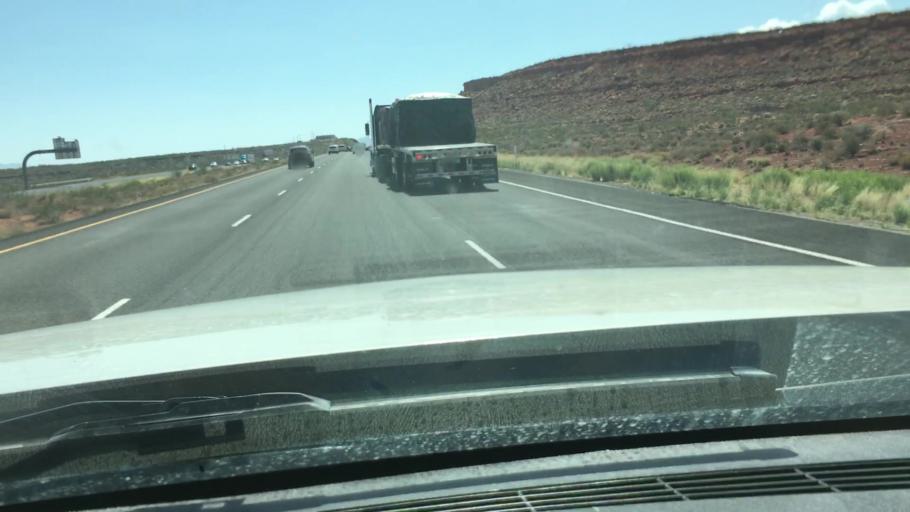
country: US
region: Utah
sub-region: Washington County
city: Washington
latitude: 37.1637
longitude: -113.4594
